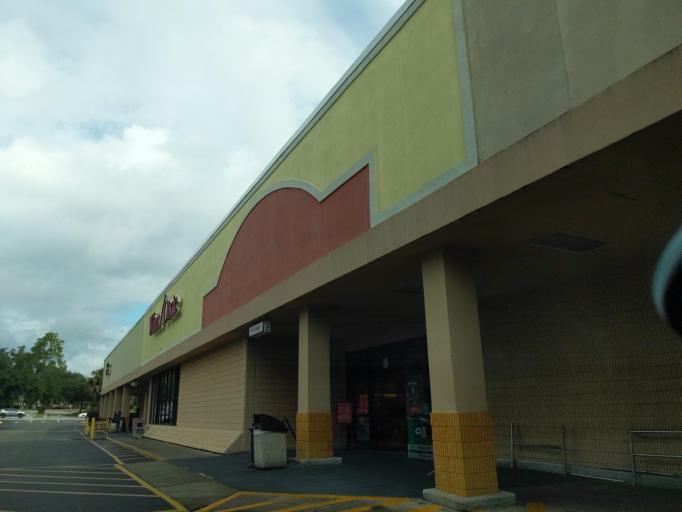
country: US
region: Florida
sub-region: Leon County
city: Tallahassee
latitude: 30.4407
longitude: -84.2603
